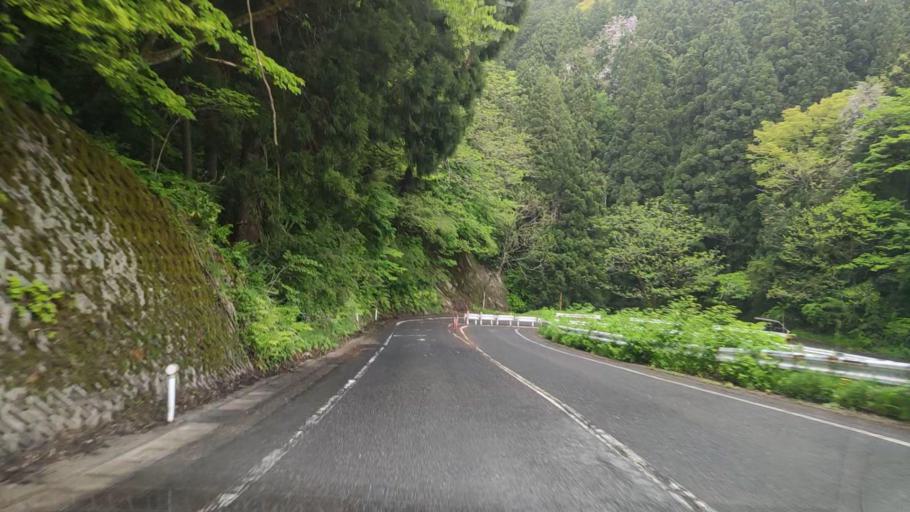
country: JP
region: Niigata
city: Gosen
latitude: 37.7157
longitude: 139.1141
